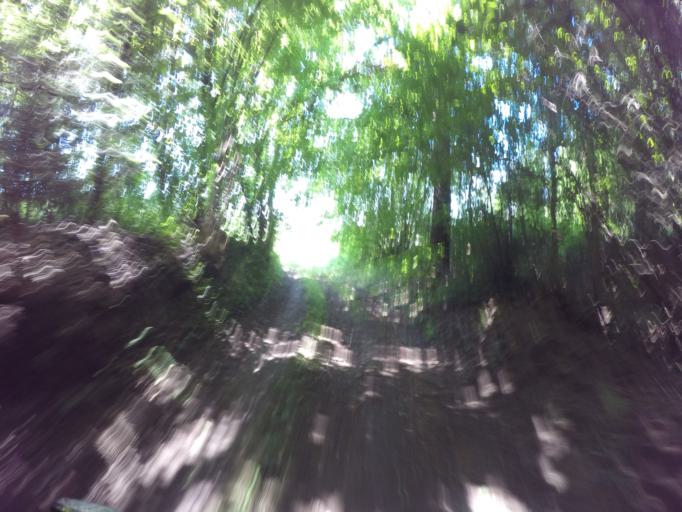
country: DE
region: Bavaria
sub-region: Lower Bavaria
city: Kumhausen
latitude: 48.5147
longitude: 12.1803
